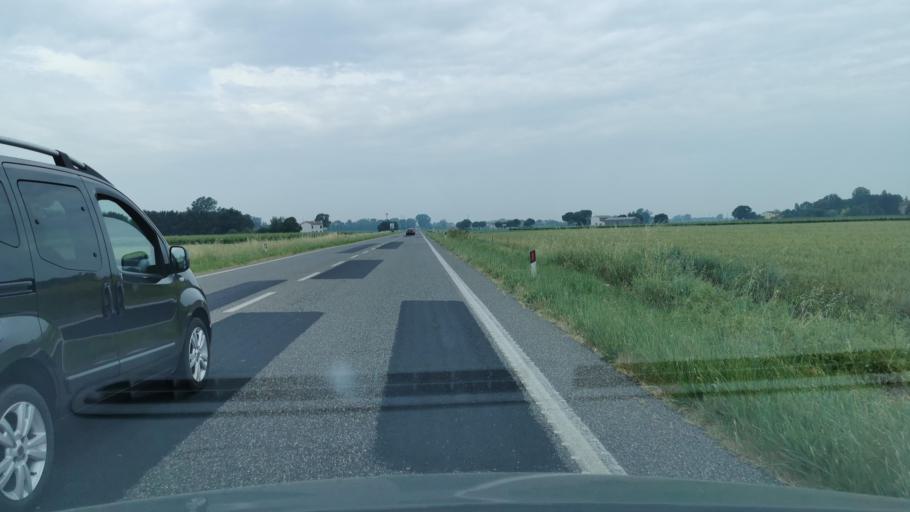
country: IT
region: Emilia-Romagna
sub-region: Provincia di Ravenna
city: Piangipane
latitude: 44.4037
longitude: 12.1007
